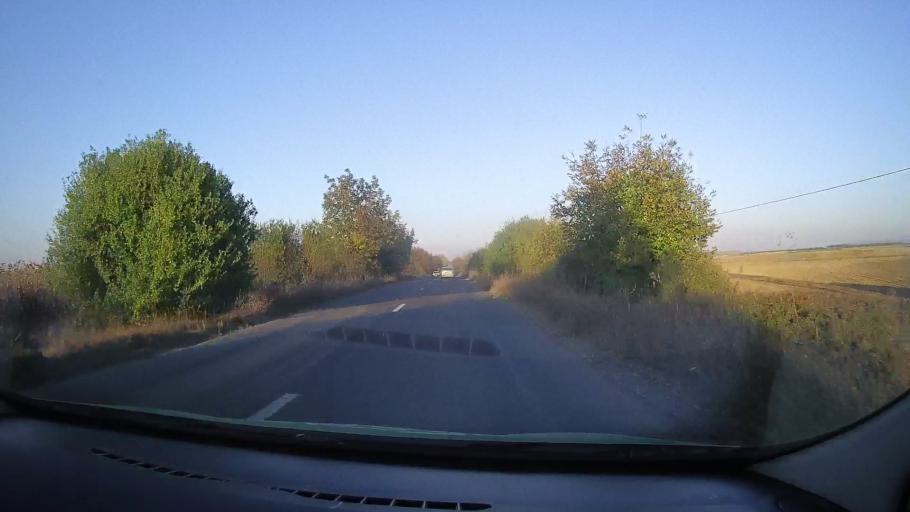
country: RO
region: Bihor
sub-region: Comuna Salard
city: Salard
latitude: 47.2005
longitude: 22.0080
